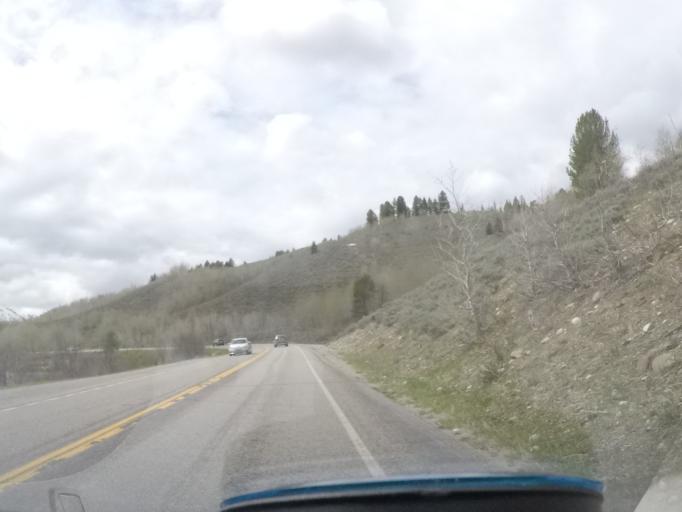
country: US
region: Wyoming
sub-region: Teton County
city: Jackson
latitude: 43.8668
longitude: -110.5508
